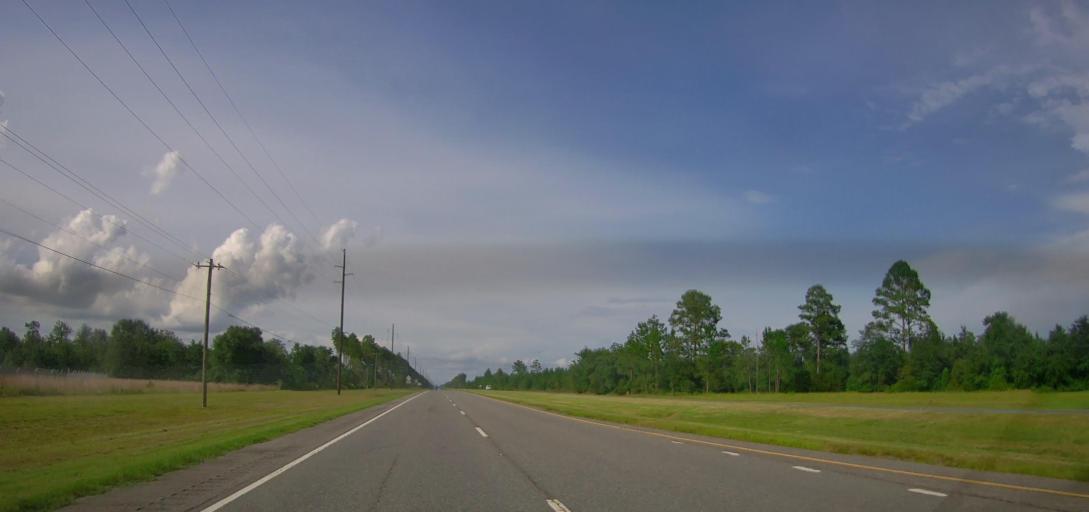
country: US
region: Georgia
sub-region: Wayne County
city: Jesup
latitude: 31.5317
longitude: -81.9837
